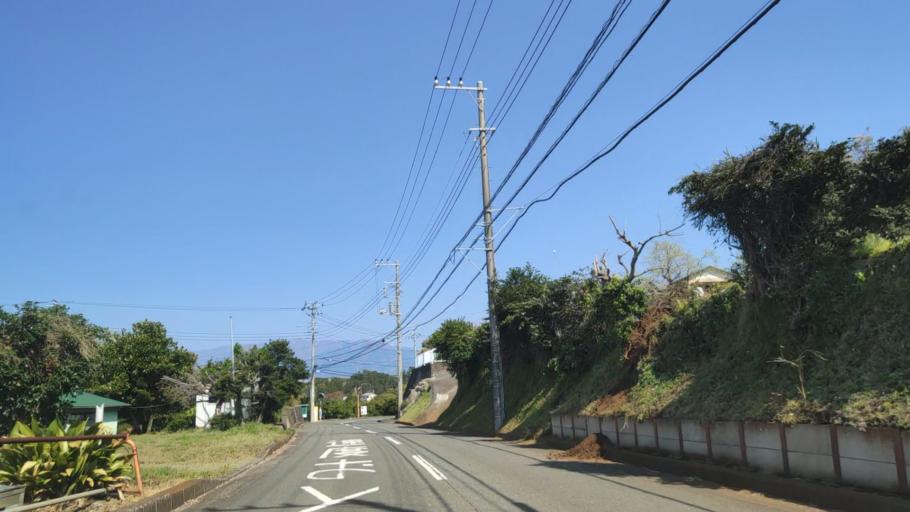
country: JP
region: Kanagawa
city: Ninomiya
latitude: 35.3232
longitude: 139.2583
